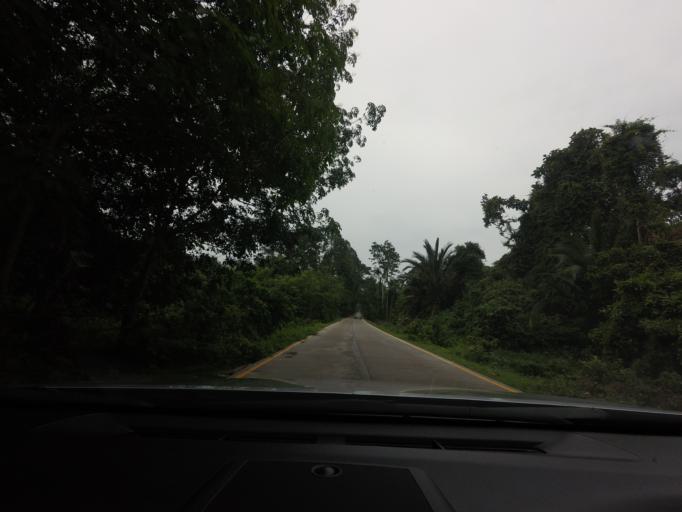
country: TH
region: Narathiwat
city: Rueso
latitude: 6.4123
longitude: 101.5264
